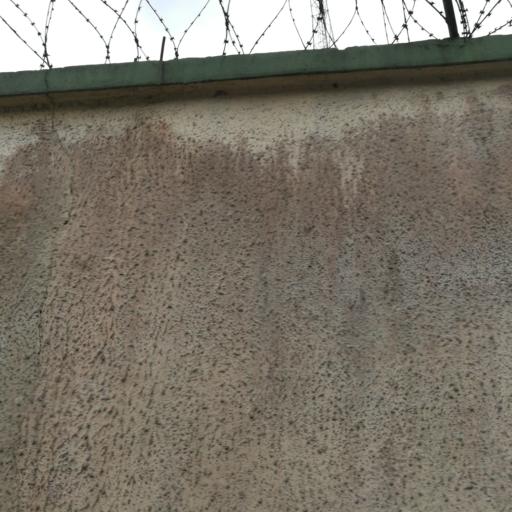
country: NG
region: Rivers
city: Port Harcourt
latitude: 4.8325
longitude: 7.0772
